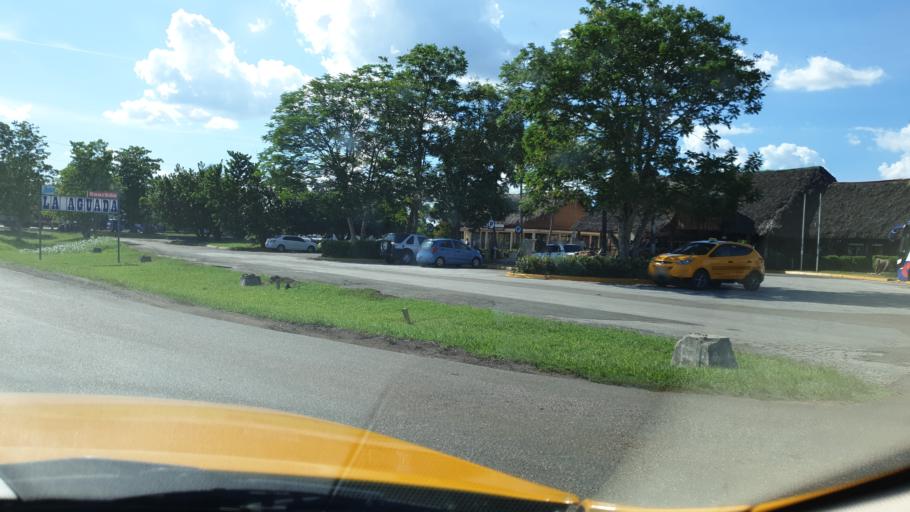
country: CU
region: Cienfuegos
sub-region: Municipio de Aguada de Pasajeros
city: Aguada de Pasajeros
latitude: 22.4045
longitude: -80.8651
